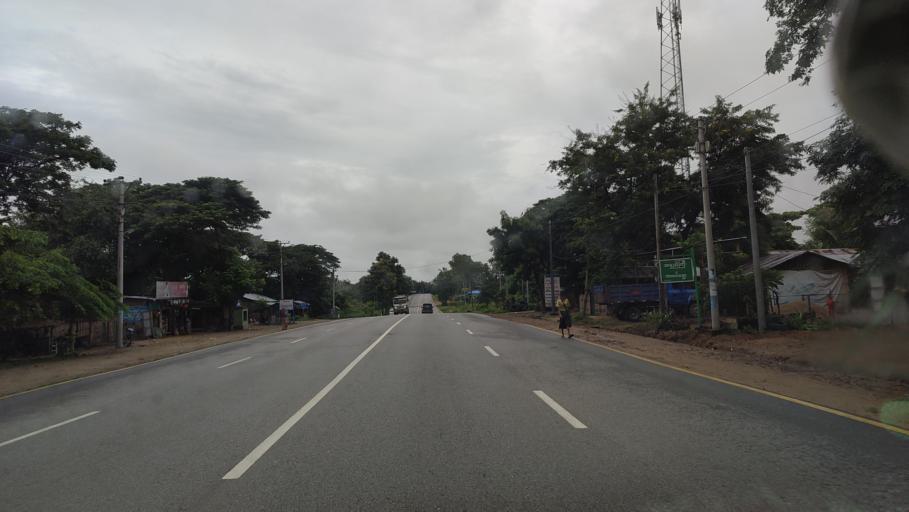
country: MM
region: Mandalay
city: Pyinmana
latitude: 19.9886
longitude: 96.2487
